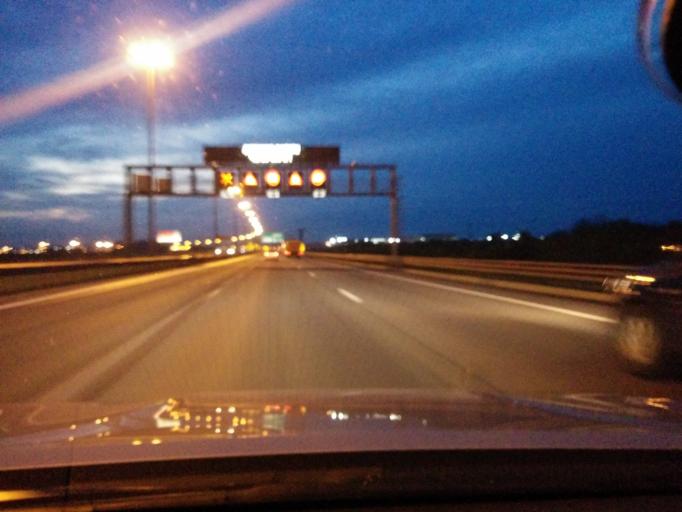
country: RU
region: Leningrad
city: Bugry
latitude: 60.0778
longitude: 30.3807
